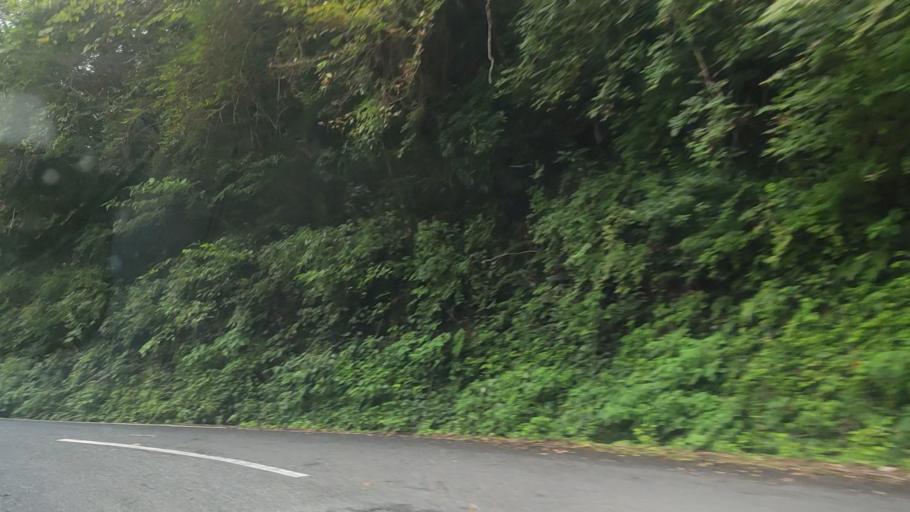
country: JP
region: Wakayama
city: Koya
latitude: 34.2491
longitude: 135.5449
